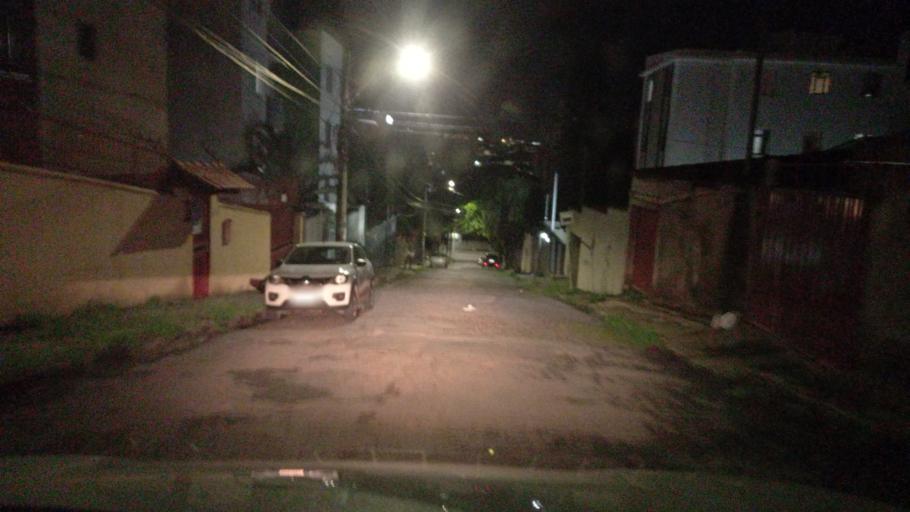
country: BR
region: Minas Gerais
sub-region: Belo Horizonte
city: Belo Horizonte
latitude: -19.9096
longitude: -43.9763
